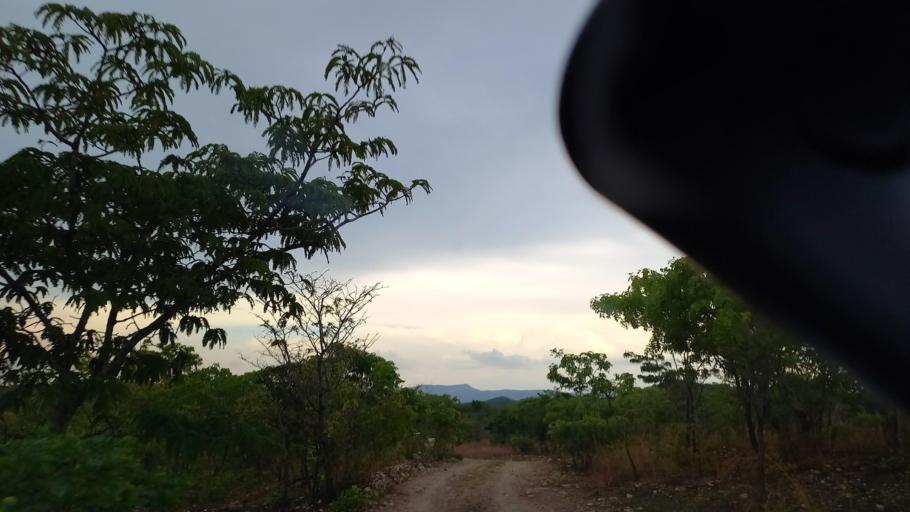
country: ZM
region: Lusaka
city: Kafue
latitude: -16.0471
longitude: 28.3204
